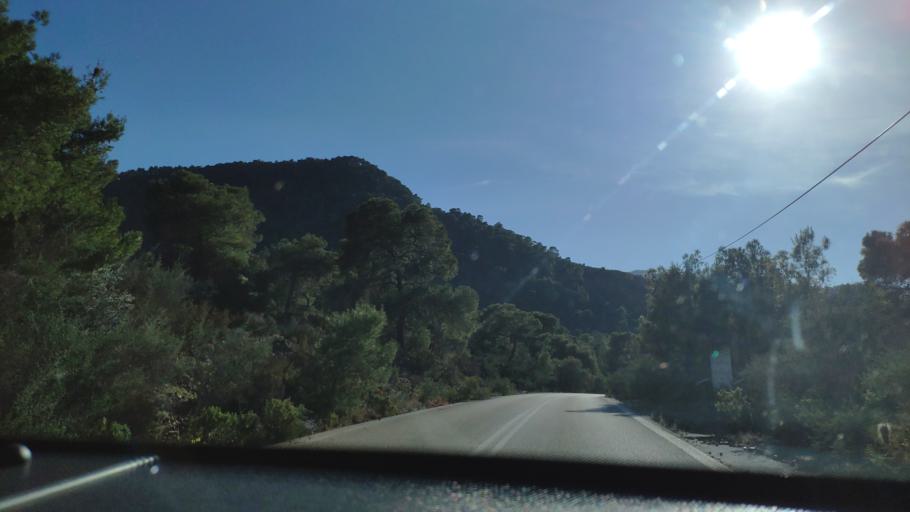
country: GR
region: Peloponnese
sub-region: Nomos Korinthias
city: Agioi Theodoroi
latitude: 38.0591
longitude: 23.0972
